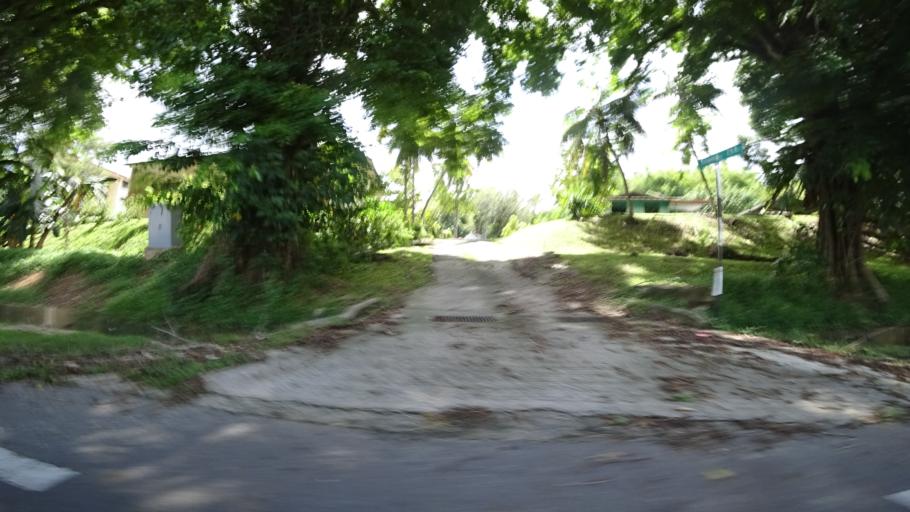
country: BN
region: Brunei and Muara
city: Bandar Seri Begawan
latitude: 4.8751
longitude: 114.9567
